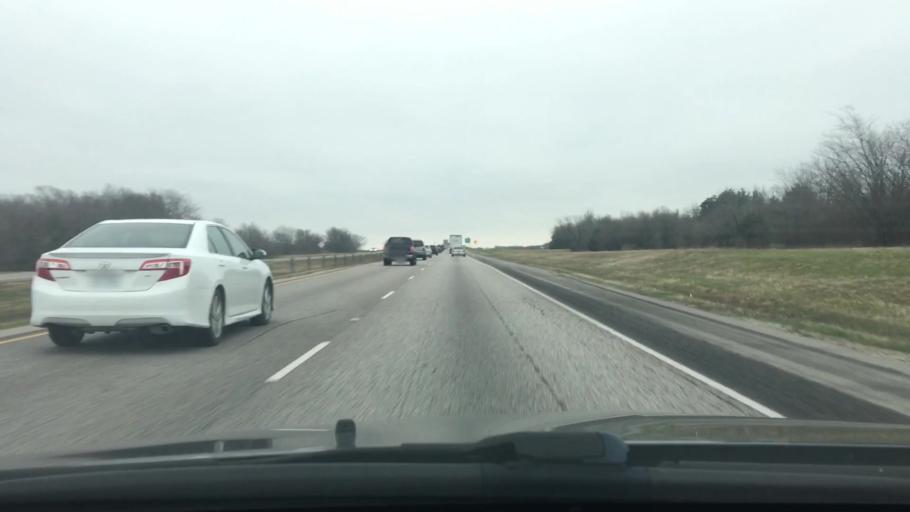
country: US
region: Texas
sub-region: Freestone County
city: Wortham
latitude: 31.8675
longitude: -96.3299
